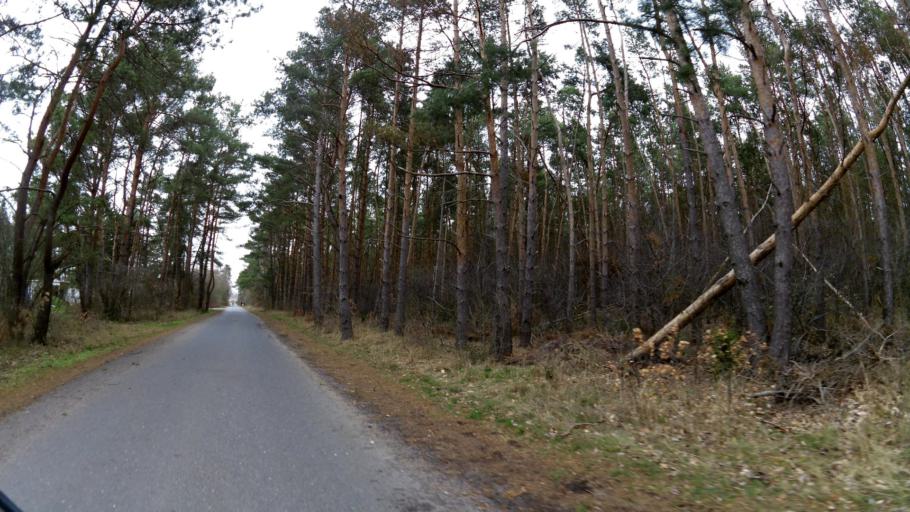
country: DE
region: Berlin
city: Bohnsdorf
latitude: 52.3831
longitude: 13.5568
